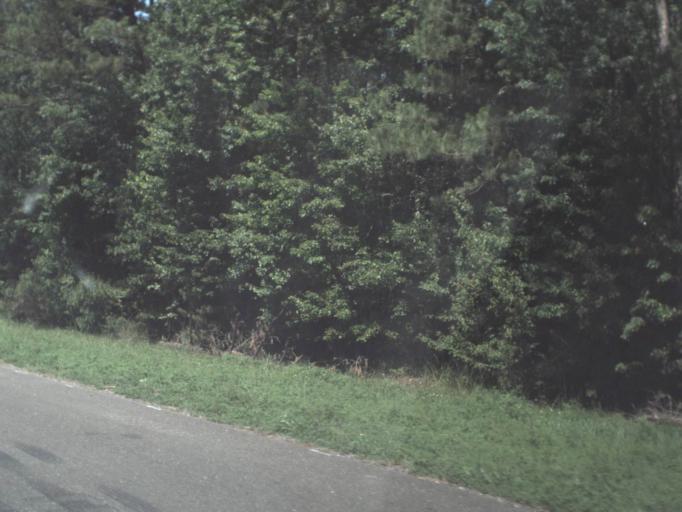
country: US
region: Florida
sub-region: Nassau County
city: Nassau Village-Ratliff
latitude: 30.4470
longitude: -81.7191
